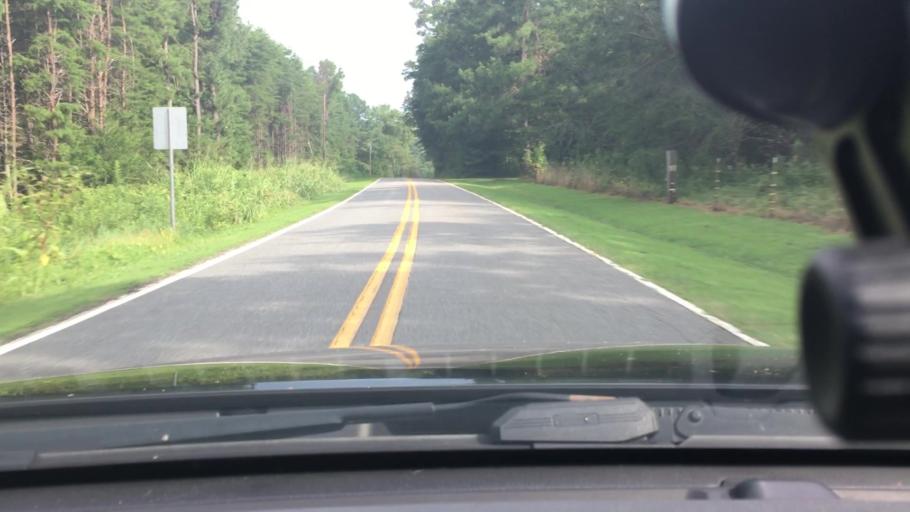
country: US
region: North Carolina
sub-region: Rutherford County
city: Rutherfordton
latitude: 35.3996
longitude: -81.9732
